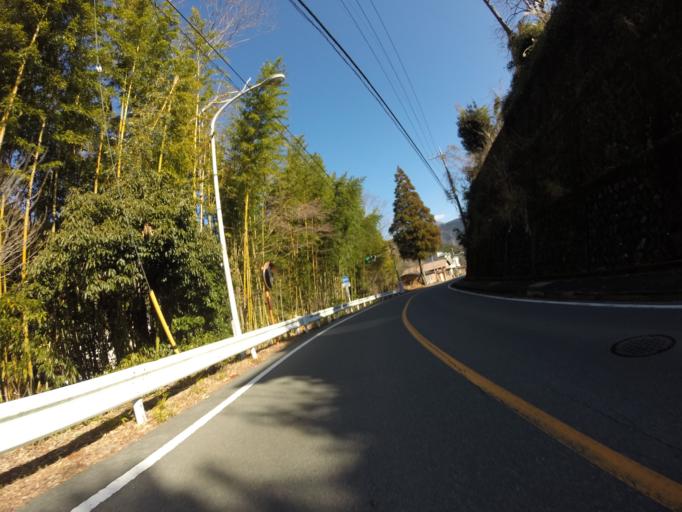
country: JP
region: Shizuoka
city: Fujinomiya
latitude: 35.3697
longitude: 138.4302
